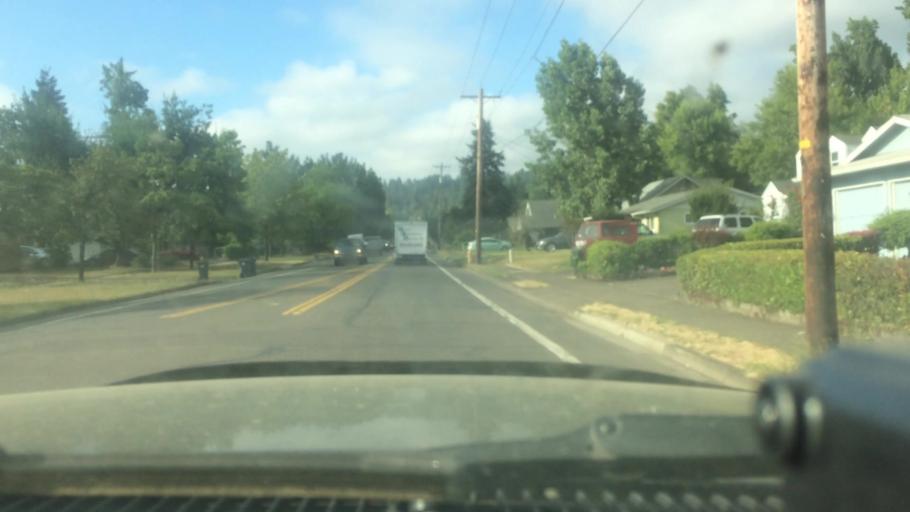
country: US
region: Oregon
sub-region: Lane County
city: Eugene
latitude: 44.0389
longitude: -123.1179
